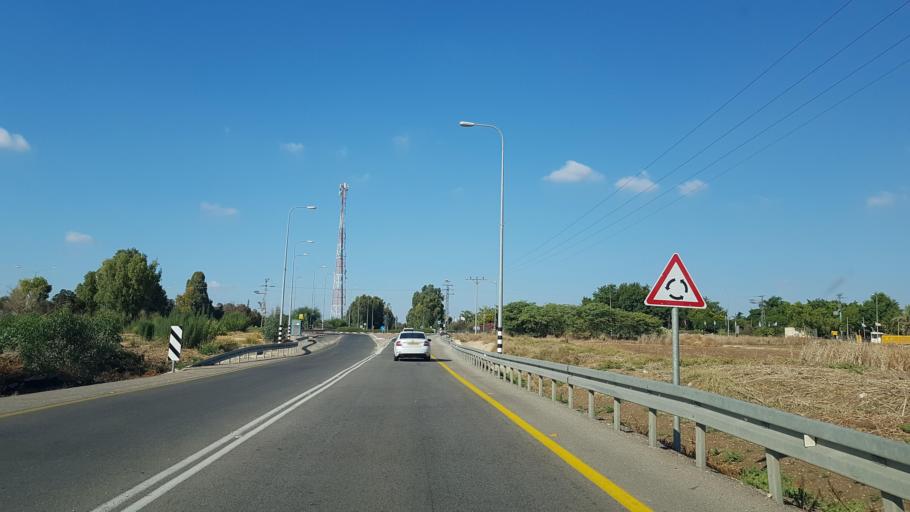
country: PS
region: West Bank
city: Tulkarm
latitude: 32.3494
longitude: 35.0131
